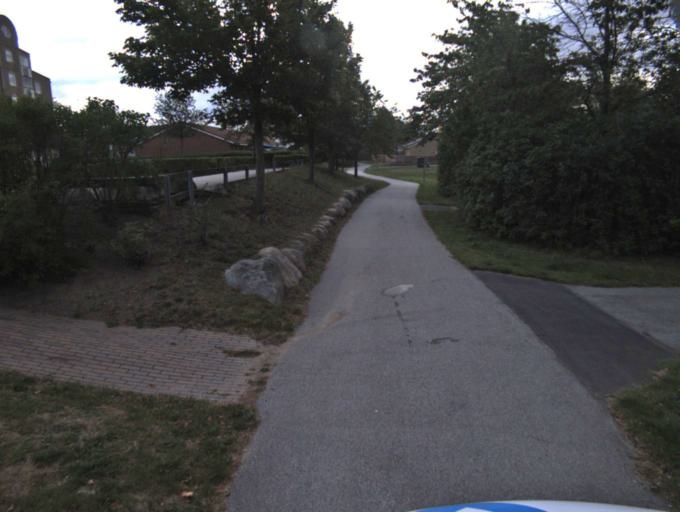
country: SE
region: Skane
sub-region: Kavlinge Kommun
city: Kaevlinge
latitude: 55.7961
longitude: 13.1343
